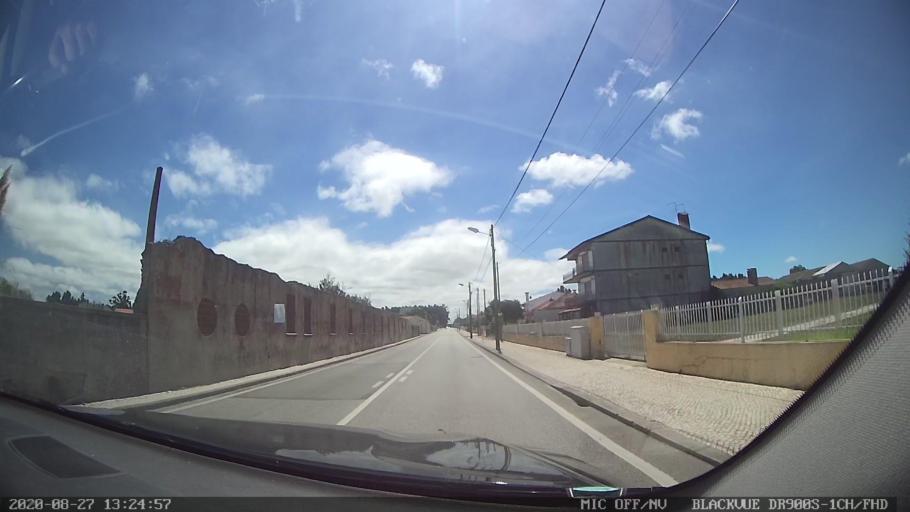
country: PT
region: Aveiro
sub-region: Vagos
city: Vagos
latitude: 40.5499
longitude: -8.6797
